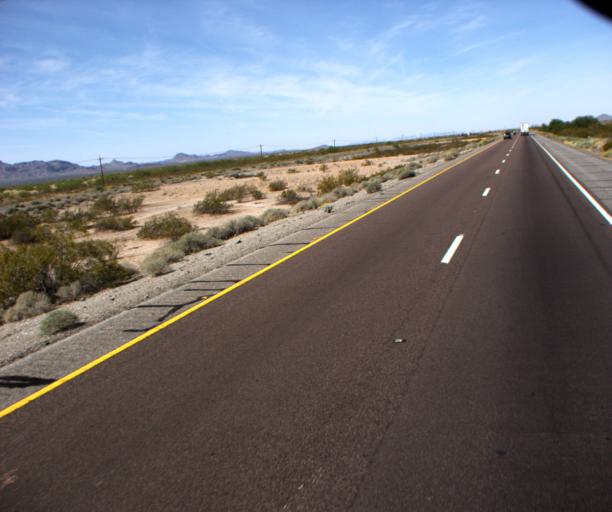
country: US
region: Arizona
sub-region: La Paz County
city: Salome
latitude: 33.5639
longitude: -113.3171
